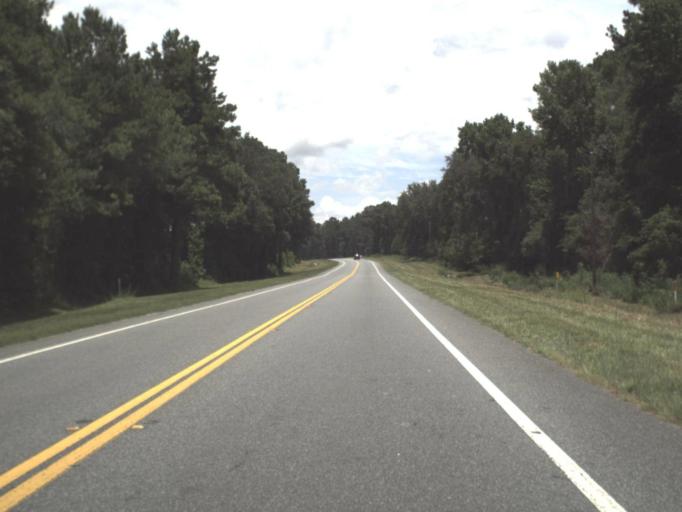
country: US
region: Florida
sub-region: Suwannee County
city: Live Oak
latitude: 30.3491
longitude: -82.9489
